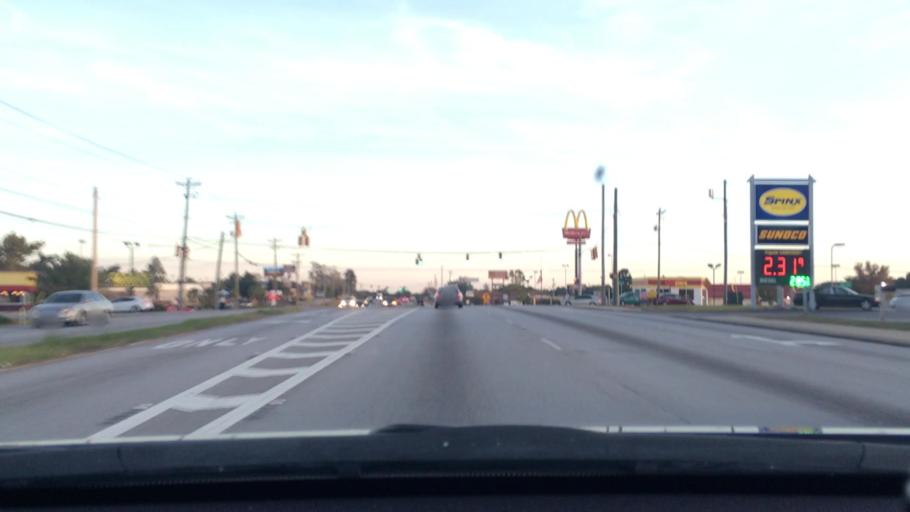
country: US
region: South Carolina
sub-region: Richland County
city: Forest Acres
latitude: 33.9663
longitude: -80.9442
